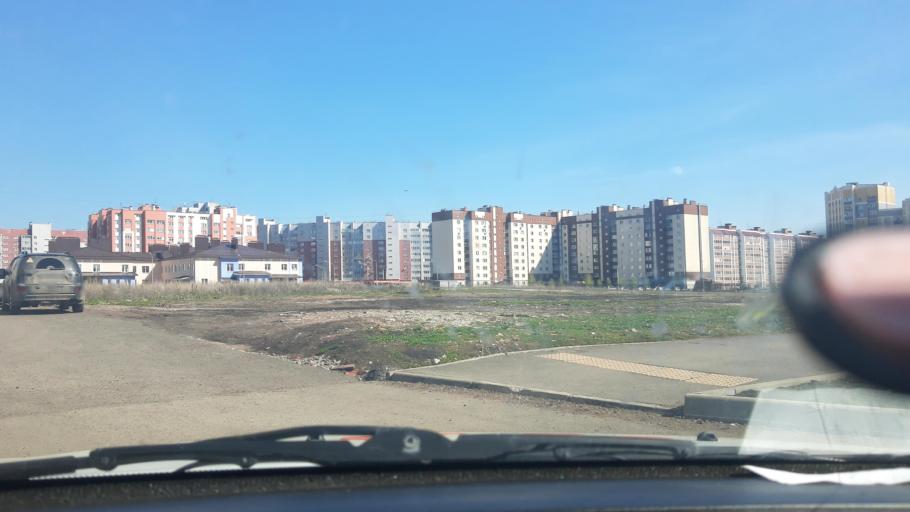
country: RU
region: Bashkortostan
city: Sterlitamak
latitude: 53.6257
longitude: 55.8965
